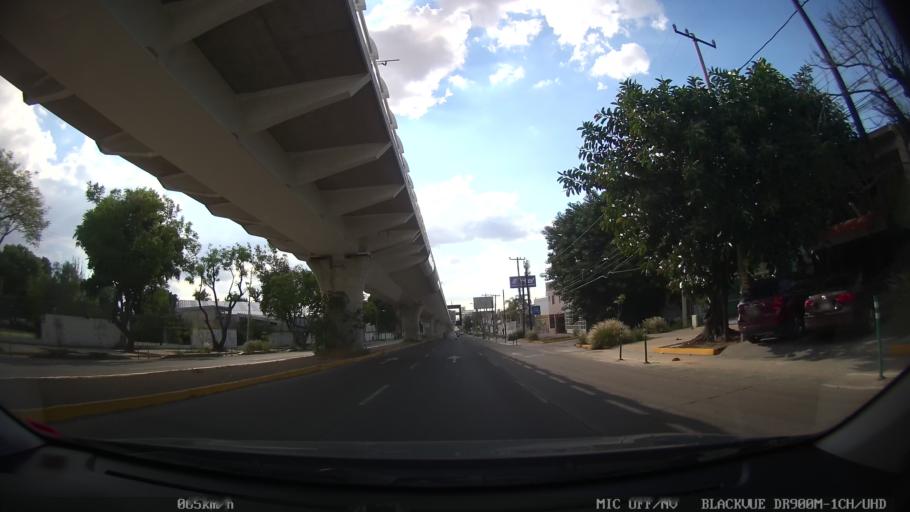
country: MX
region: Jalisco
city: Tlaquepaque
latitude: 20.6575
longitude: -103.3204
